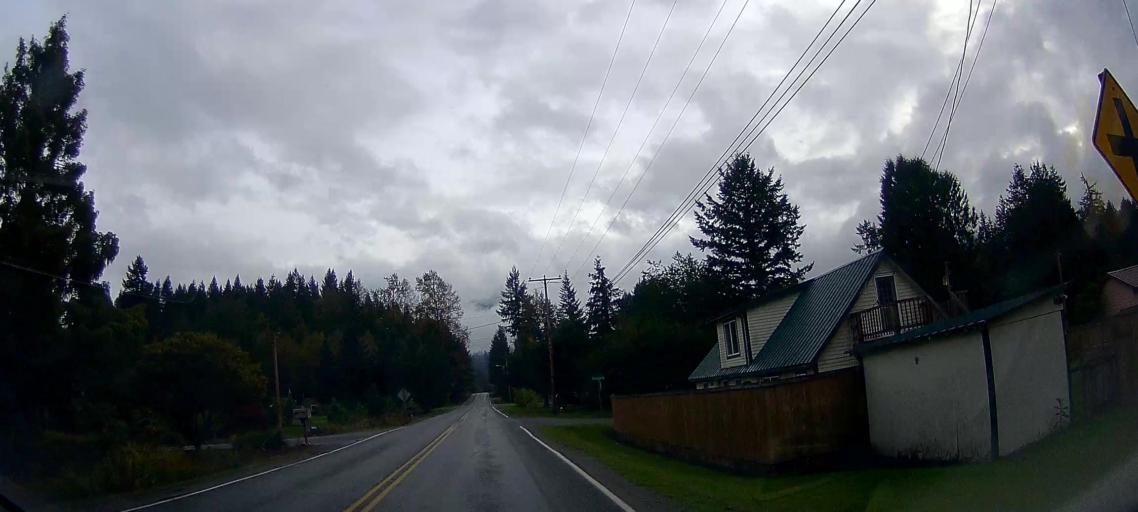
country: US
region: Washington
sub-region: Snohomish County
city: Darrington
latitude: 48.5359
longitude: -121.7661
